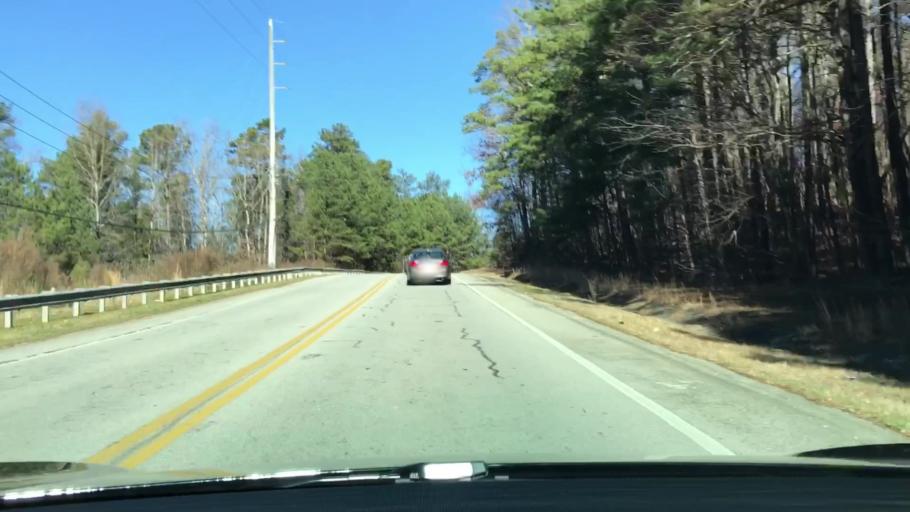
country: US
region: Georgia
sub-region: Gwinnett County
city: Sugar Hill
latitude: 34.1470
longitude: -84.0515
